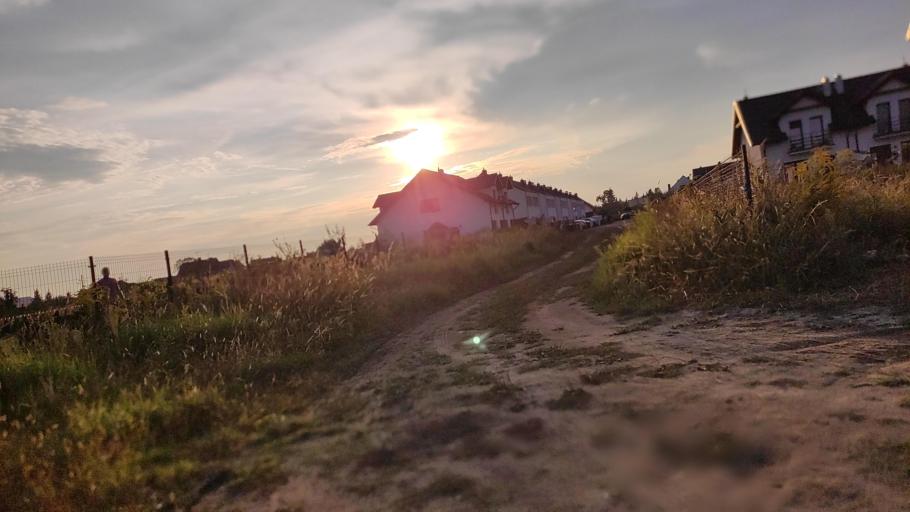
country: PL
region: Greater Poland Voivodeship
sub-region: Powiat poznanski
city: Kleszczewo
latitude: 52.3916
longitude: 17.1619
